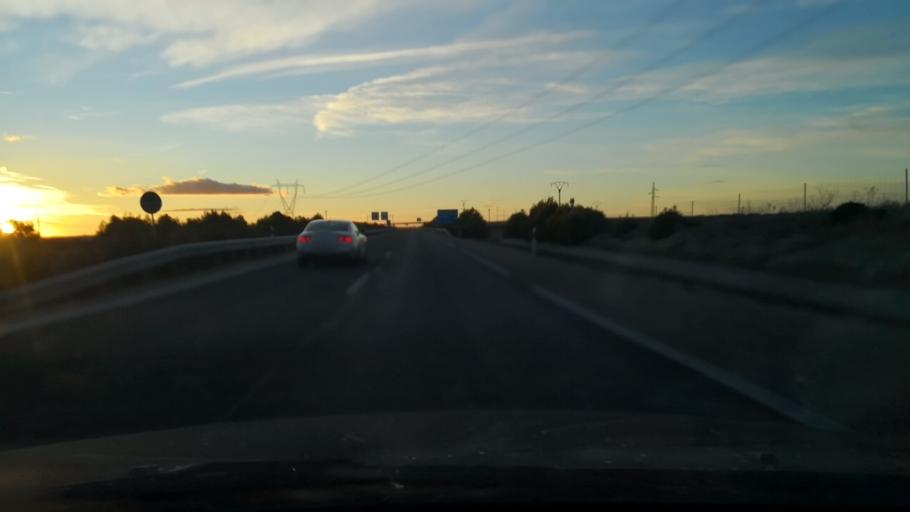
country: ES
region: Castille and Leon
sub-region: Provincia de Valladolid
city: Tordesillas
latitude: 41.5042
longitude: -5.0297
